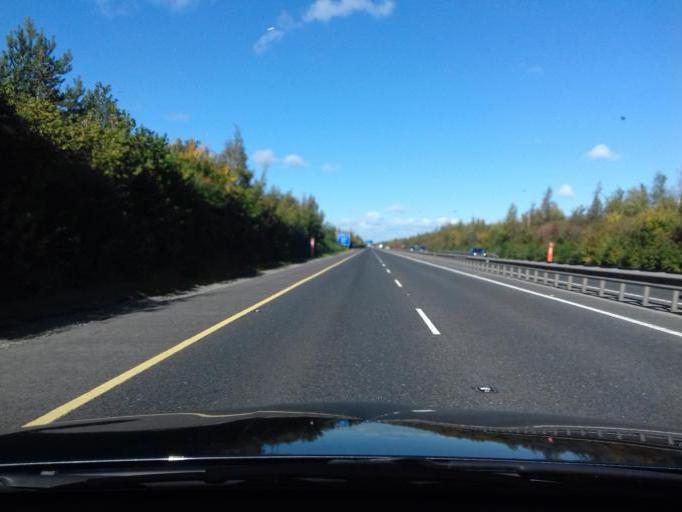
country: IE
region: Leinster
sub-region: An Mhi
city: Ashbourne
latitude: 53.4692
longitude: -6.3631
